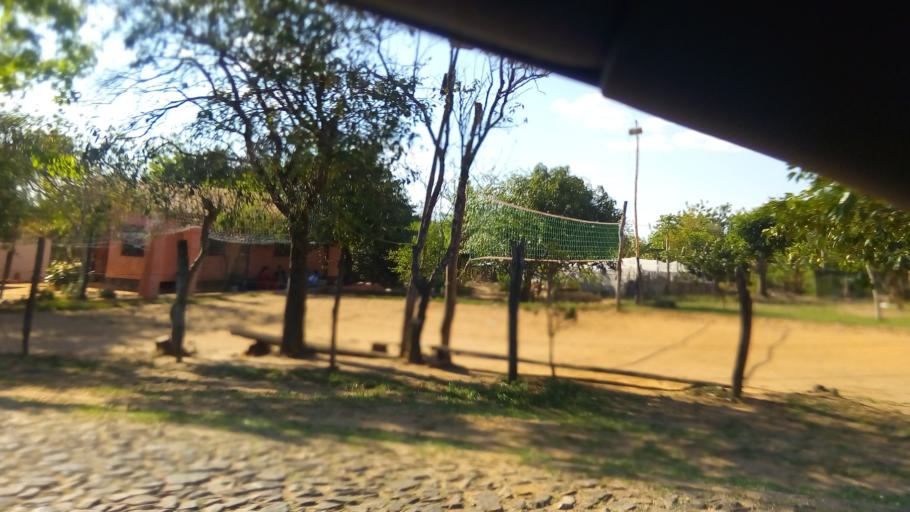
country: PY
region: Cordillera
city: Arroyos y Esteros
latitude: -24.9967
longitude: -57.1650
